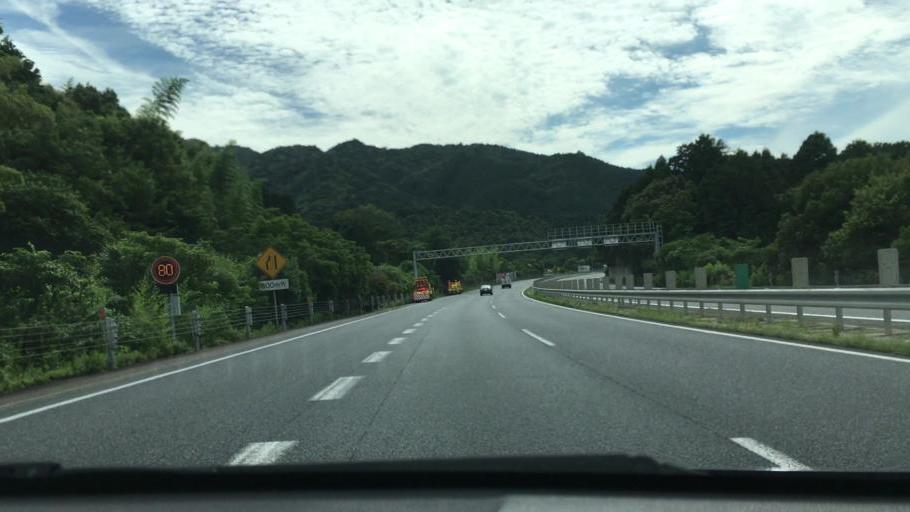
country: JP
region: Yamaguchi
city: Ogori-shimogo
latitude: 34.1301
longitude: 131.4429
